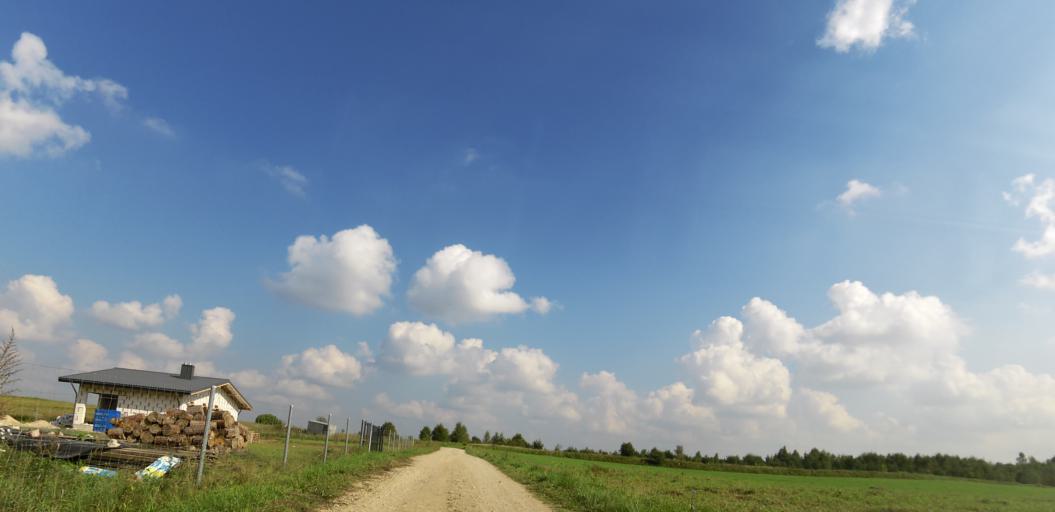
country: LT
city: Grigiskes
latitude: 54.7614
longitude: 25.0773
